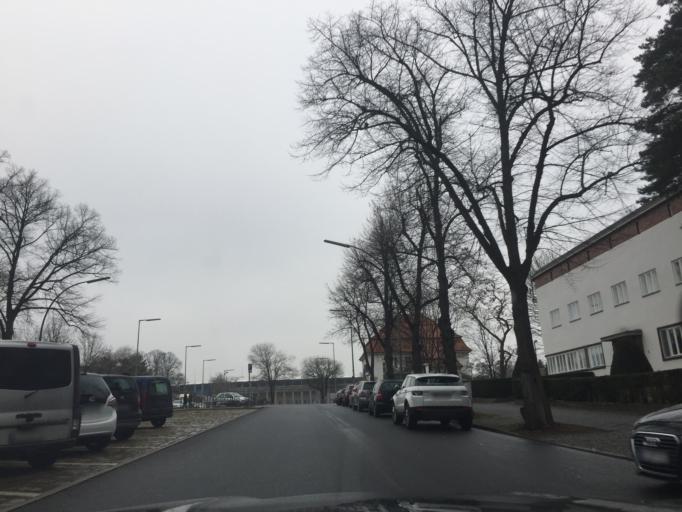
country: DE
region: Berlin
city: Haselhorst
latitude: 52.5101
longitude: 13.2412
